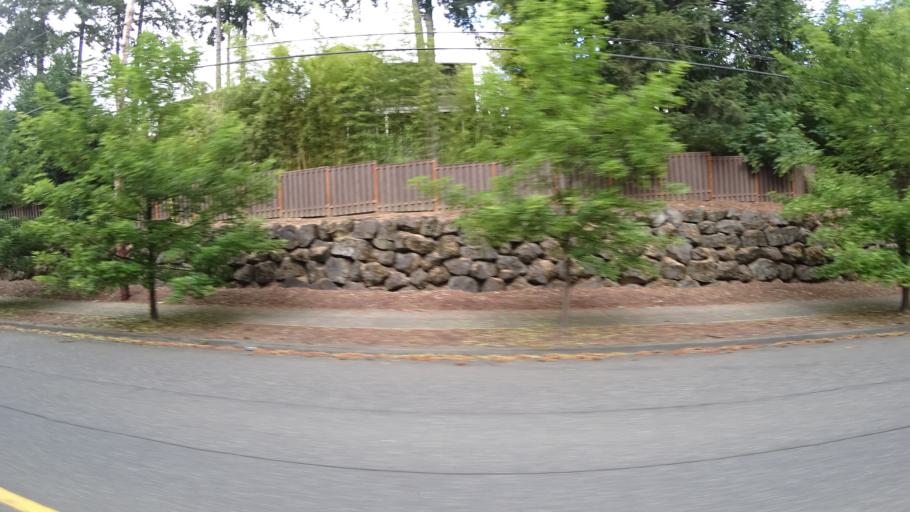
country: US
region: Oregon
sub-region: Clackamas County
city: Lake Oswego
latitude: 45.4375
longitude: -122.6937
